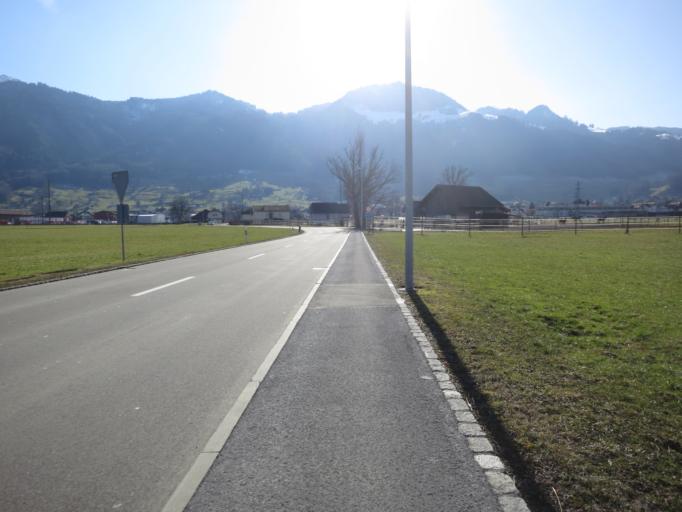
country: CH
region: Schwyz
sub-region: Bezirk March
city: Reichenburg
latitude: 47.1752
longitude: 8.9862
